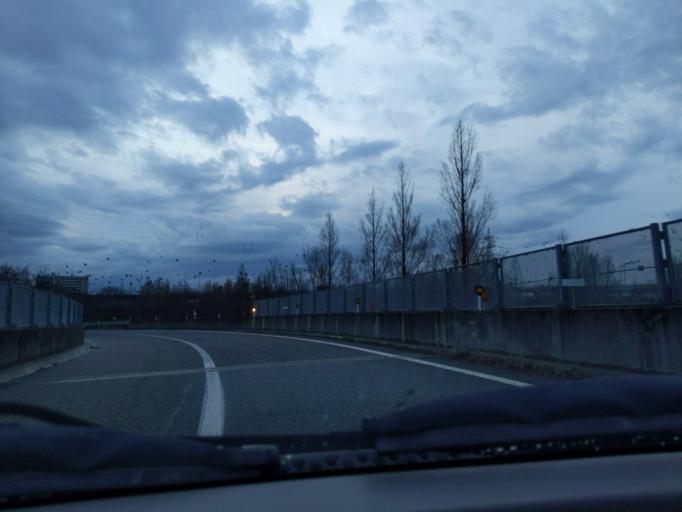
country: JP
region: Niigata
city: Niigata-shi
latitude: 37.8721
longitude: 139.0431
